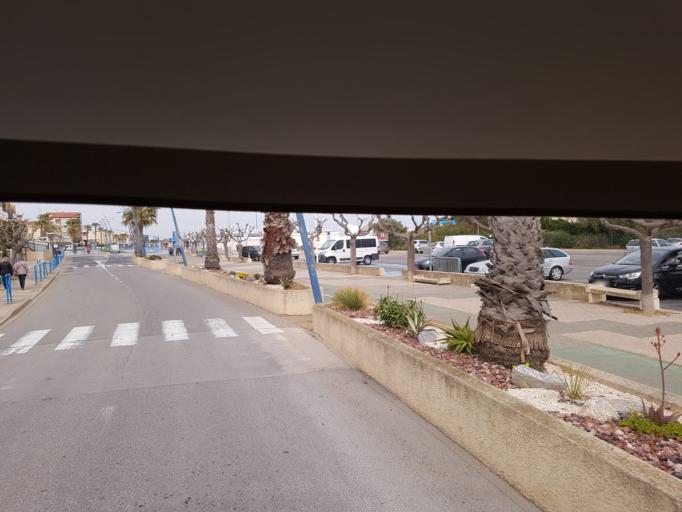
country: FR
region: Languedoc-Roussillon
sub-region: Departement de l'Aude
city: Fleury
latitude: 43.1773
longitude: 3.1893
